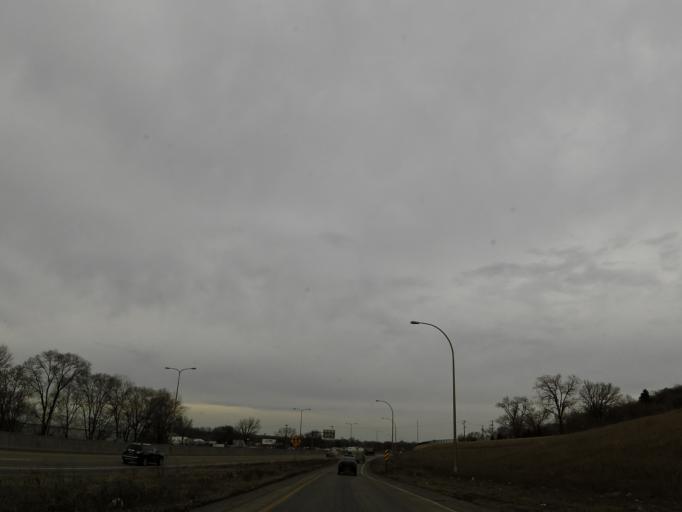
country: US
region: Minnesota
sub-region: Washington County
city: Saint Paul Park
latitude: 44.8531
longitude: -92.9923
